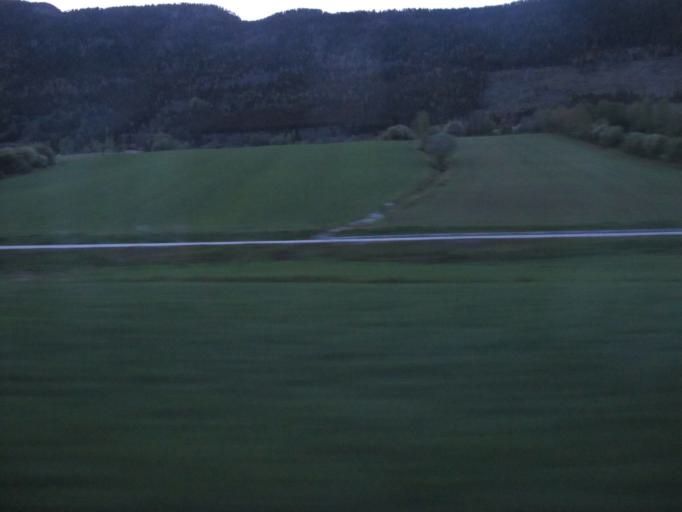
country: NO
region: Oppland
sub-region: Nord-Fron
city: Vinstra
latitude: 61.6587
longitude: 9.7331
